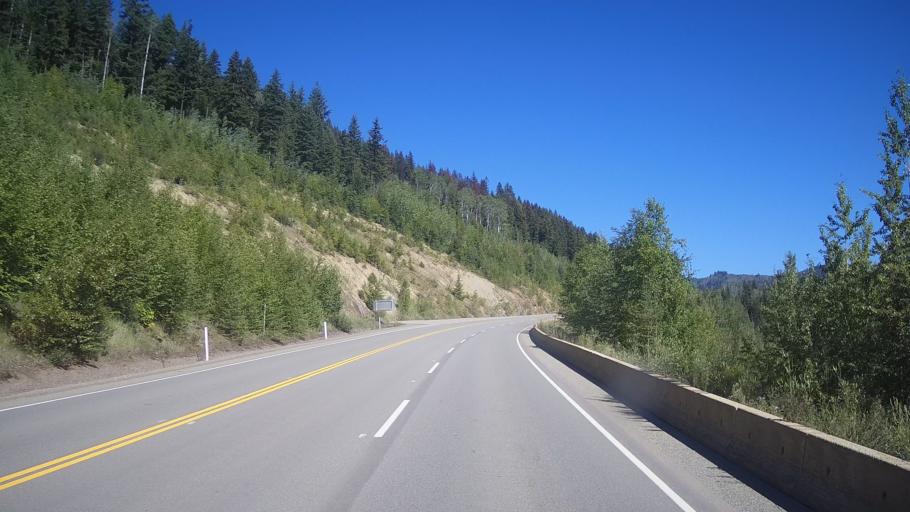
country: CA
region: British Columbia
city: Kamloops
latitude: 51.4700
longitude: -120.2546
